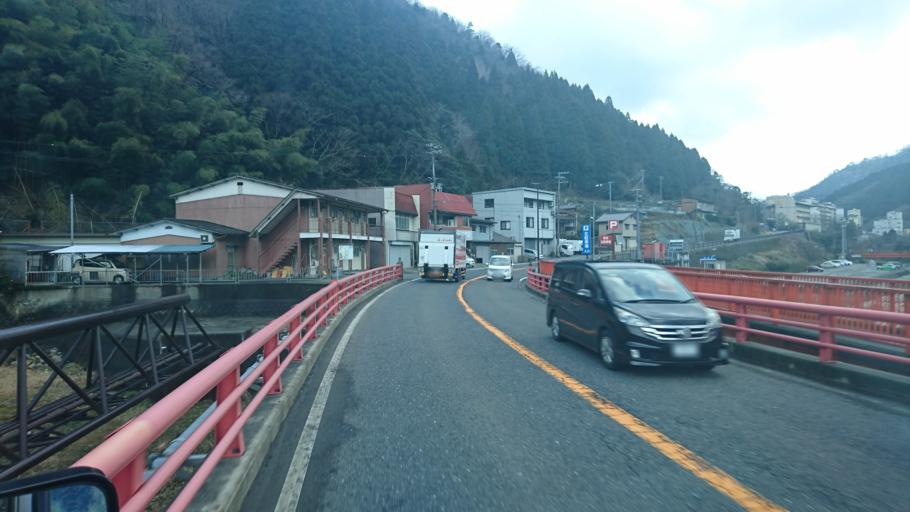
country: JP
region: Tottori
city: Tottori
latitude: 35.5604
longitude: 134.4855
